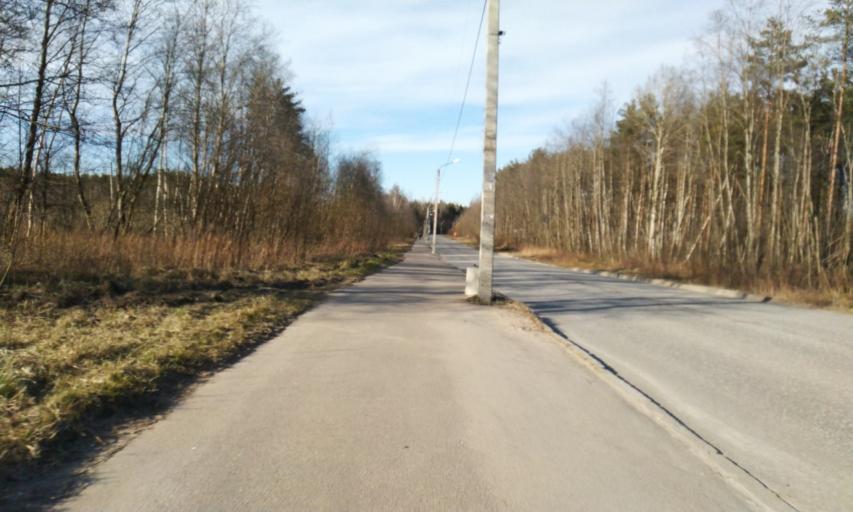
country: RU
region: Leningrad
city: Novoye Devyatkino
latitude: 60.1135
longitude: 30.4859
